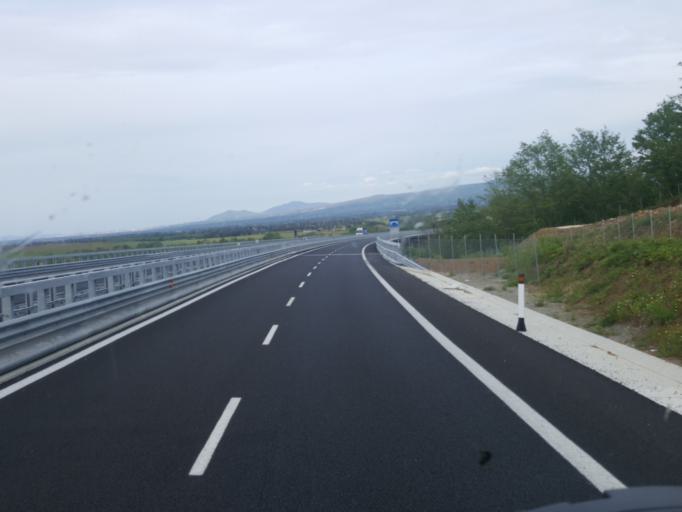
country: IT
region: Latium
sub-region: Provincia di Viterbo
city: Monte Romano
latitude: 42.2956
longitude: 11.9467
